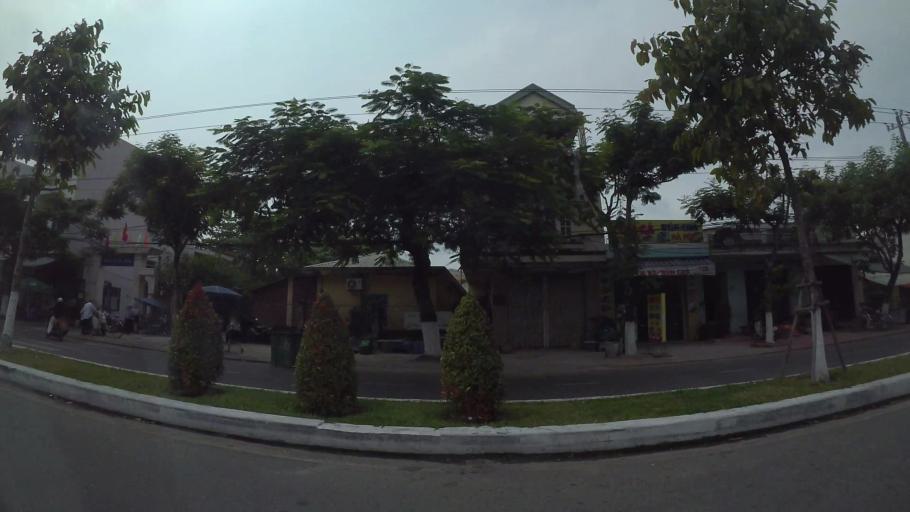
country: VN
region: Da Nang
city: Da Nang
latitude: 16.0956
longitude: 108.2447
